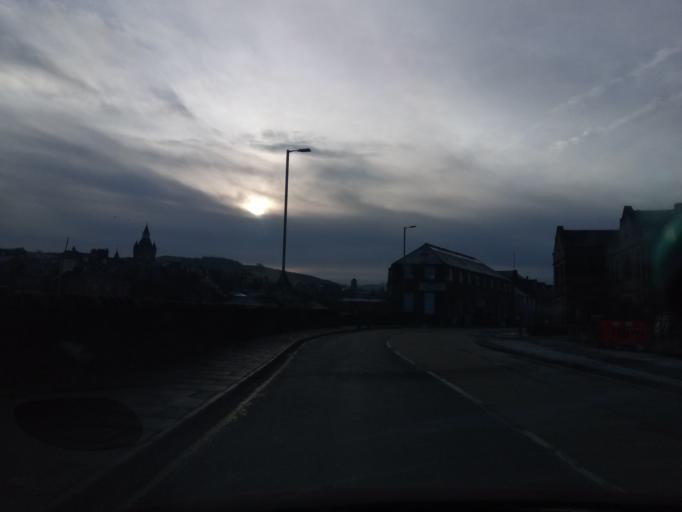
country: GB
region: Scotland
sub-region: The Scottish Borders
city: Hawick
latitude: 55.4249
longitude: -2.7880
